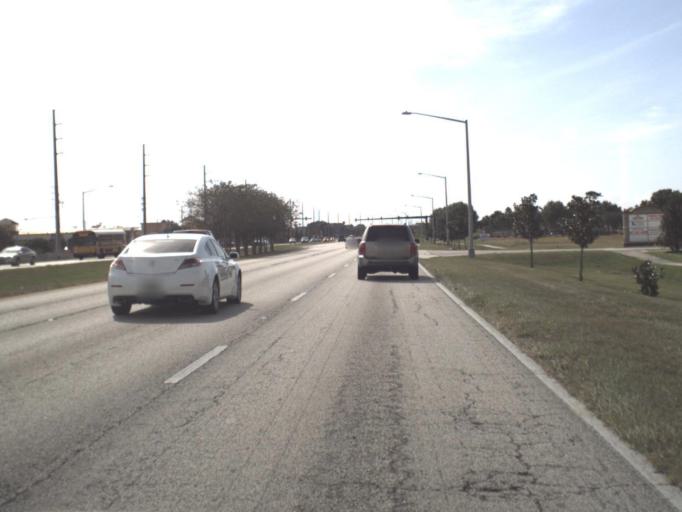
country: US
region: Florida
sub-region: Orange County
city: Williamsburg
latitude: 28.3912
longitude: -81.4252
